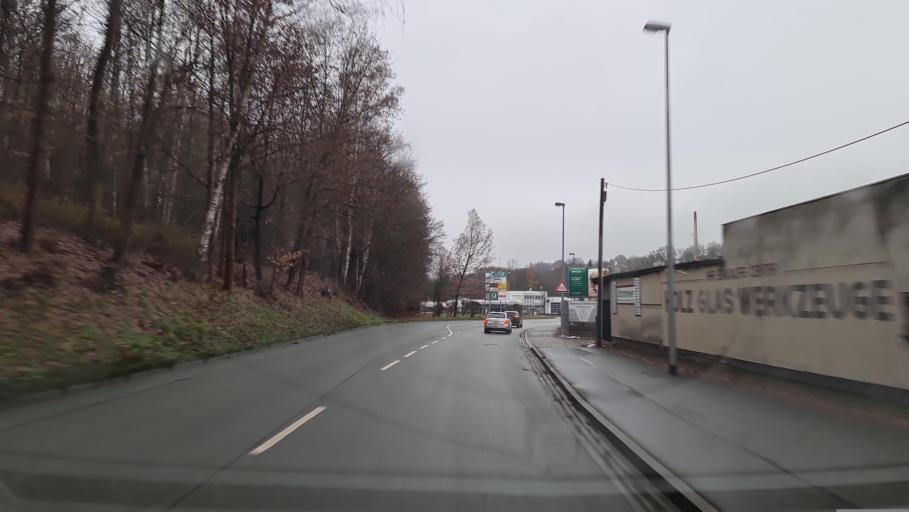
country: DE
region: Saxony
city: Mylau
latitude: 50.6179
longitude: 12.2762
